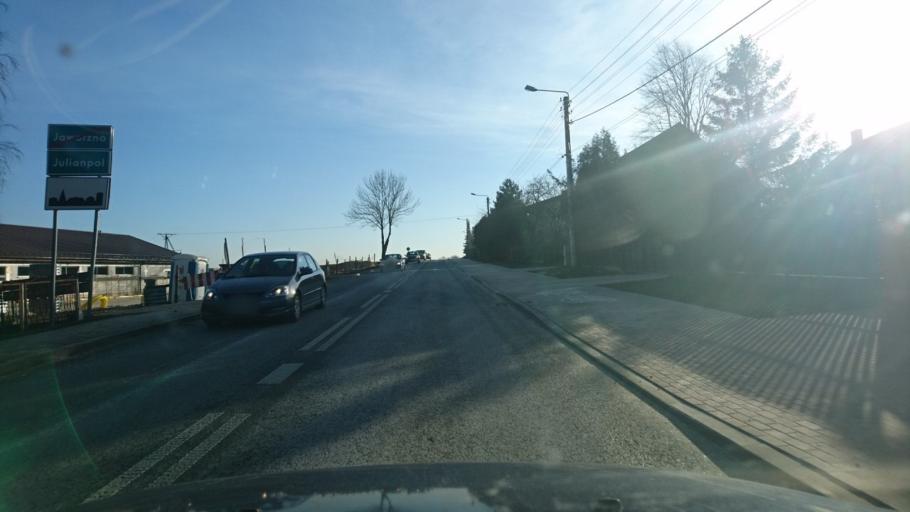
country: PL
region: Silesian Voivodeship
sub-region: Powiat klobucki
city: Starokrzepice
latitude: 51.0209
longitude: 18.6511
